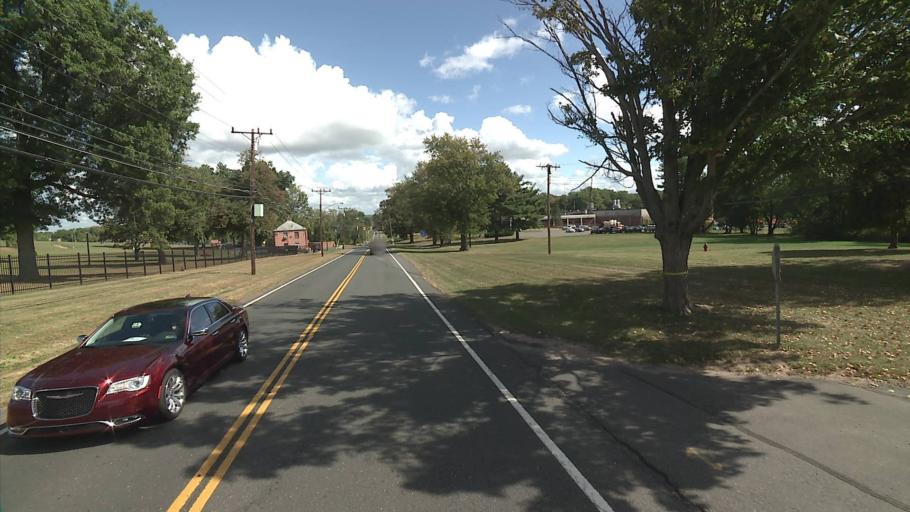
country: US
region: Connecticut
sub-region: Middlesex County
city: Cromwell
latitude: 41.6531
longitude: -72.6528
